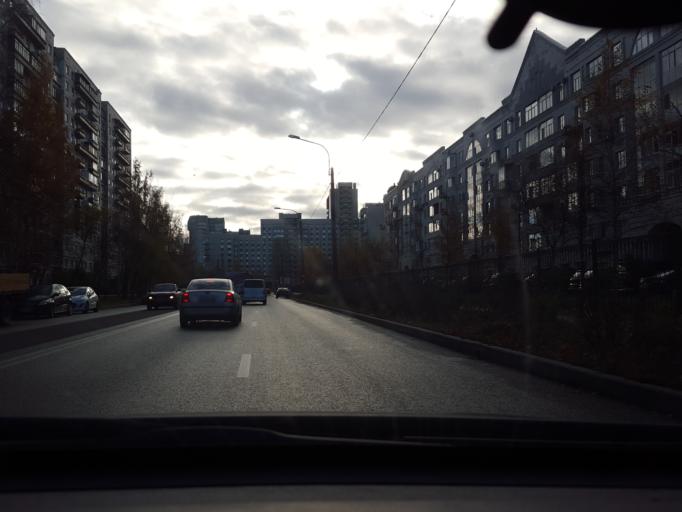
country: RU
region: St.-Petersburg
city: Ozerki
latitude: 60.0465
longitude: 30.3189
